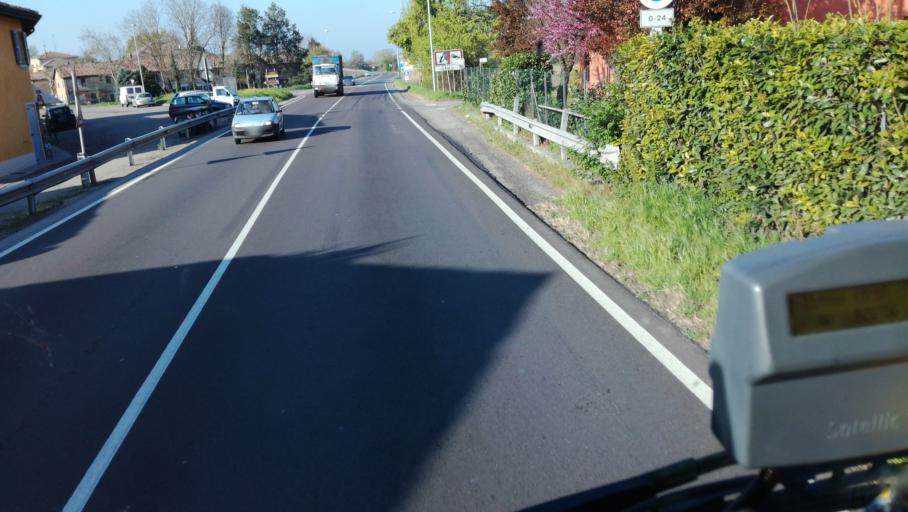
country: IT
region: Emilia-Romagna
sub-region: Provincia di Modena
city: Villanova
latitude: 44.6761
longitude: 10.9331
